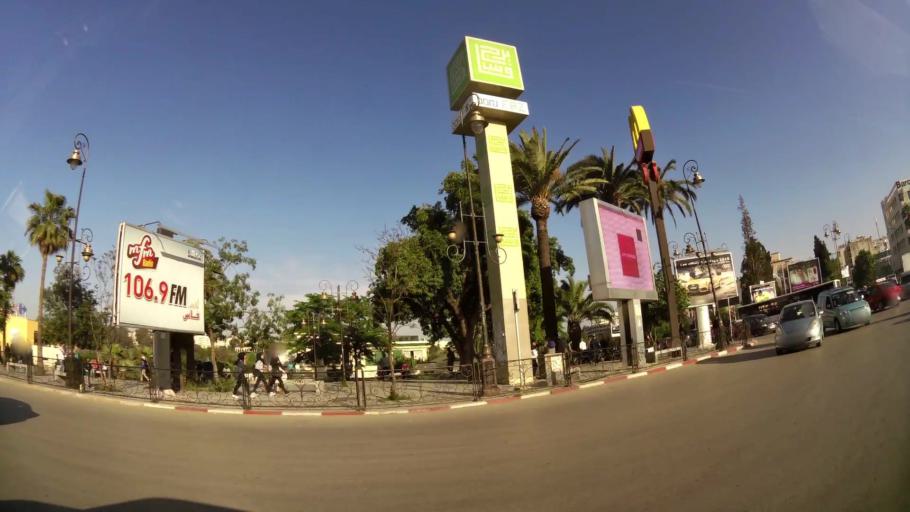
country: MA
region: Fes-Boulemane
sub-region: Fes
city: Fes
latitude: 34.0447
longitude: -4.9967
